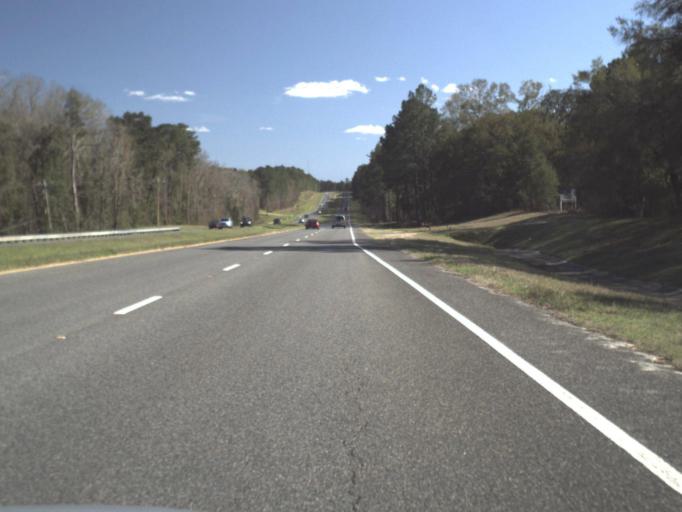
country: US
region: Florida
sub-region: Gadsden County
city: Midway
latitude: 30.5328
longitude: -84.4743
